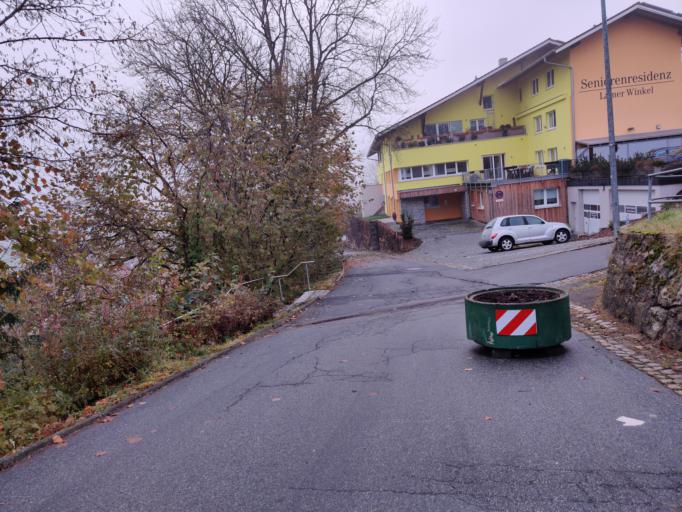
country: DE
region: Bavaria
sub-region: Upper Palatinate
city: Lam
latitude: 49.1961
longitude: 13.0520
